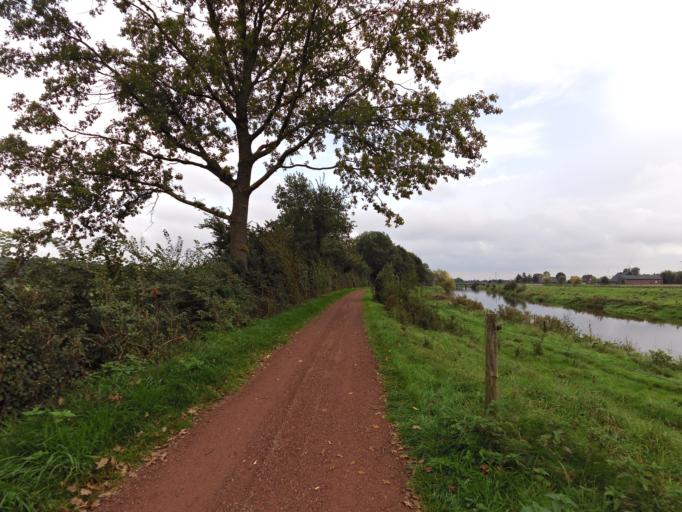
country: DE
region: North Rhine-Westphalia
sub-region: Regierungsbezirk Munster
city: Isselburg
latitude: 51.8463
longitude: 6.4972
